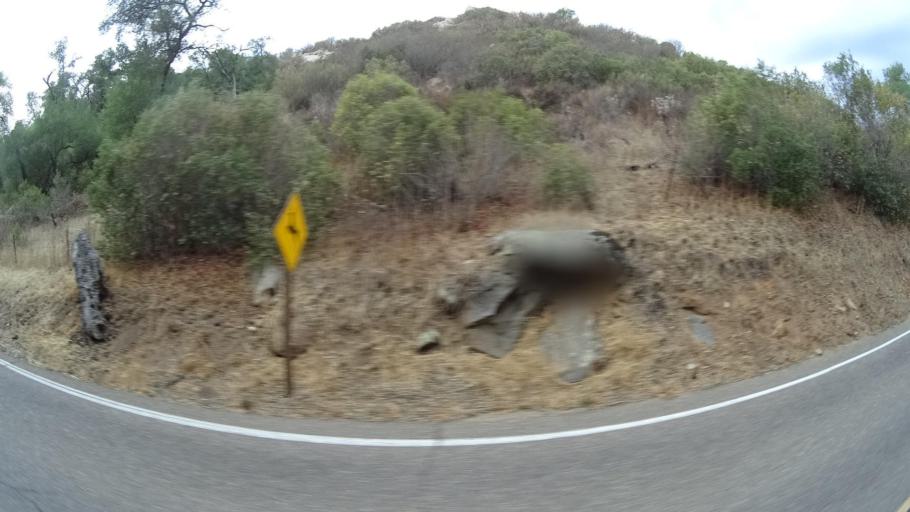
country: US
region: California
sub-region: San Diego County
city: Ramona
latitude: 32.9782
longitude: -116.9199
